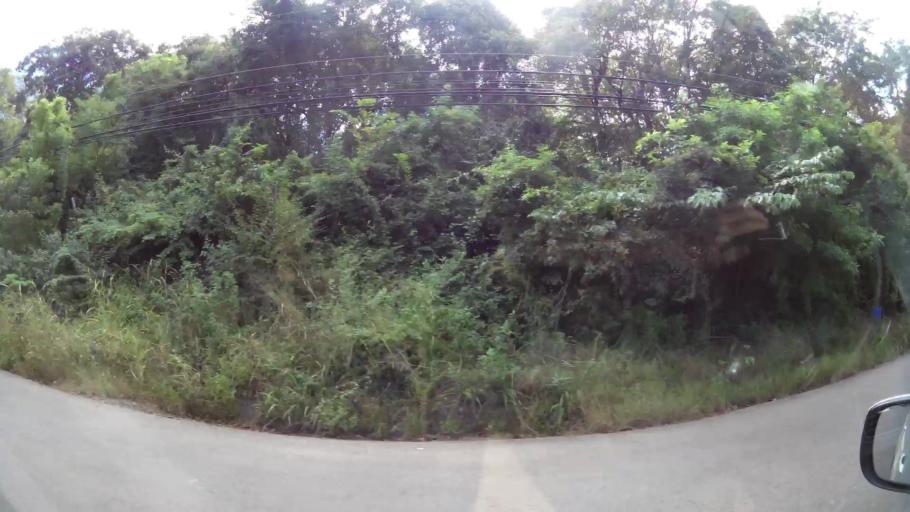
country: CR
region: Guanacaste
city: Santa Cruz
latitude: 10.3076
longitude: -85.8351
